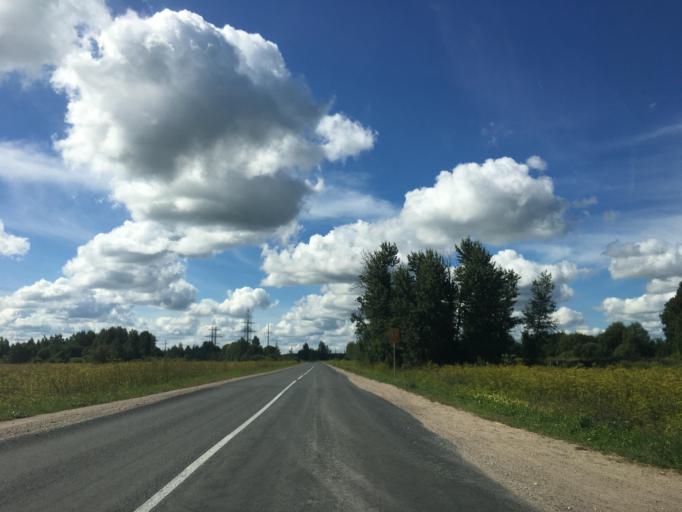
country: RU
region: Pskov
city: Pskov
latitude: 57.7775
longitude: 28.1664
